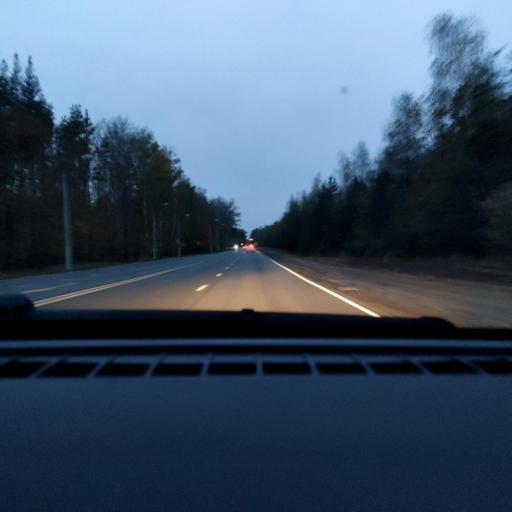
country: RU
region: Voronezj
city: Somovo
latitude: 51.6878
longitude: 39.2920
